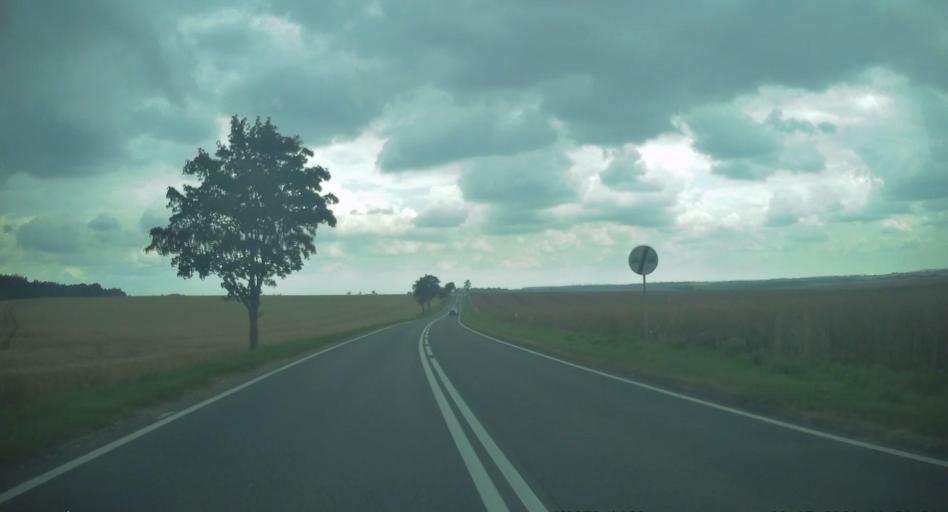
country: PL
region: Opole Voivodeship
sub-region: Powiat prudnicki
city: Moszczanka
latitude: 50.4226
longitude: 17.4567
